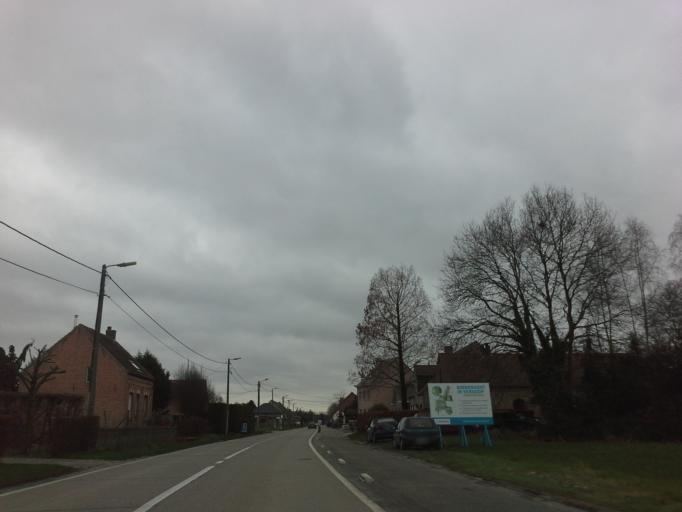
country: BE
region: Flanders
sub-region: Provincie Antwerpen
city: Hulshout
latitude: 51.1029
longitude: 4.7951
